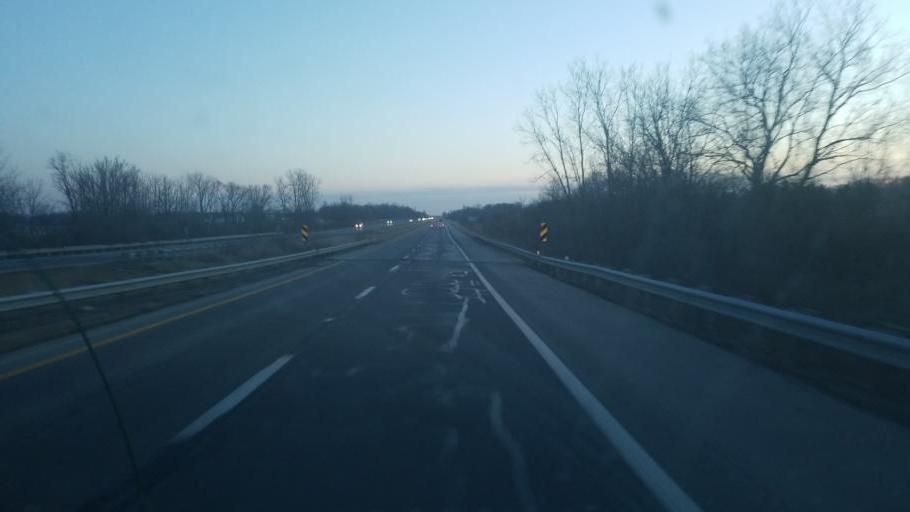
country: US
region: Ohio
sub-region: Marion County
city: Marion
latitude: 40.5471
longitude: -83.0746
